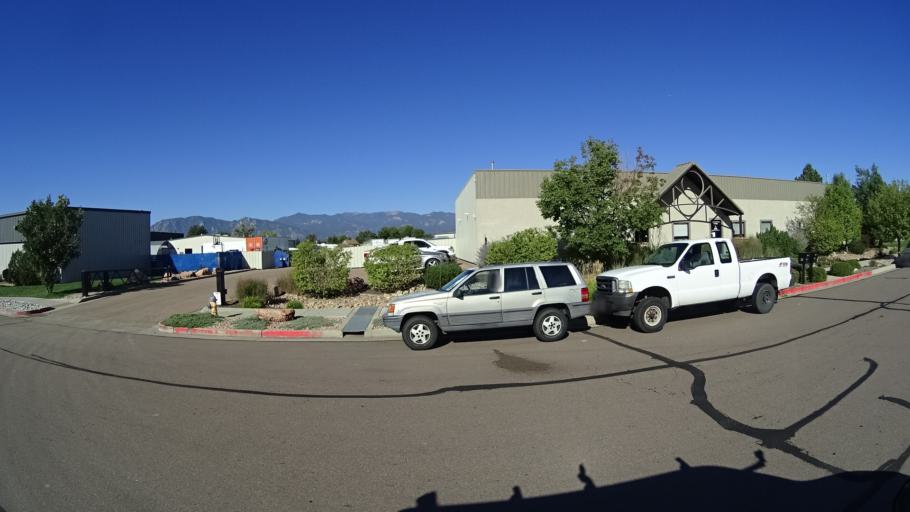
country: US
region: Colorado
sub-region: El Paso County
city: Stratmoor
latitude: 38.8025
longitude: -104.7328
